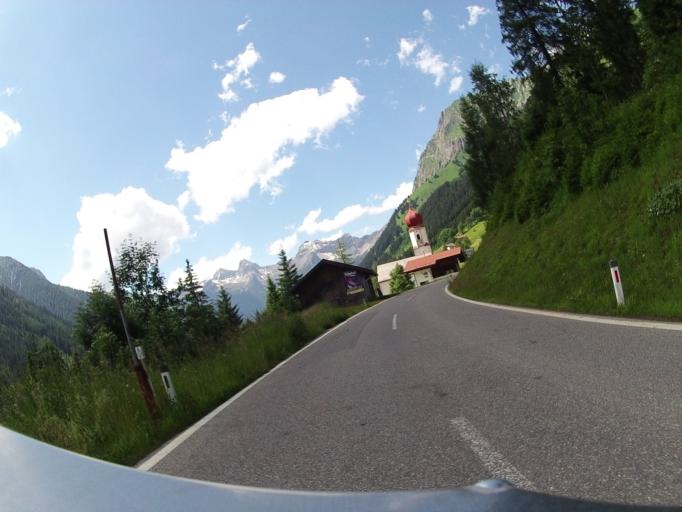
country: AT
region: Tyrol
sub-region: Politischer Bezirk Reutte
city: Elmen
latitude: 47.3067
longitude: 10.5870
